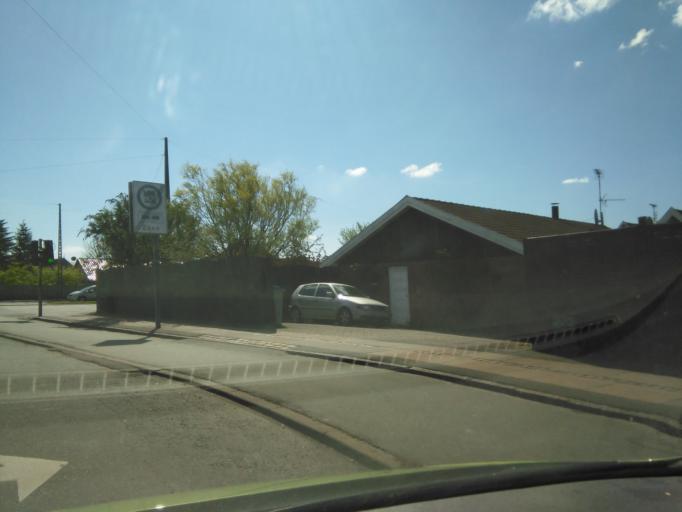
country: DK
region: Capital Region
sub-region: Tarnby Kommune
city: Tarnby
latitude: 55.6429
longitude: 12.5983
